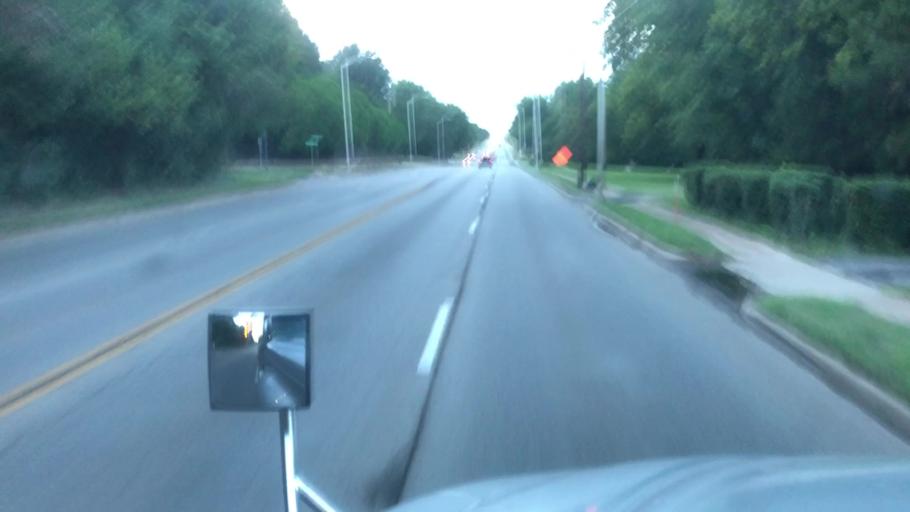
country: US
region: Oklahoma
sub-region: Kay County
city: Ponca City
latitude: 36.7163
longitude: -97.0672
